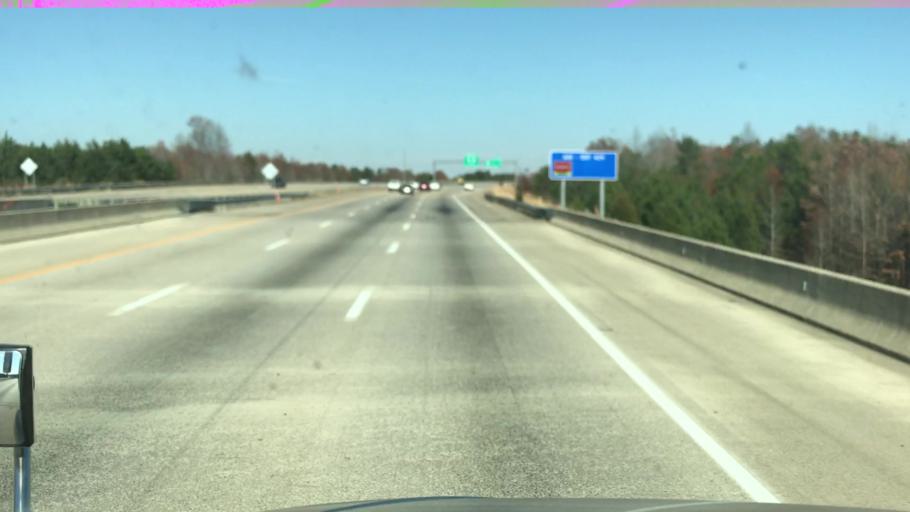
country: US
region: North Carolina
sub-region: Wake County
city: Knightdale
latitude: 35.7969
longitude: -78.4317
